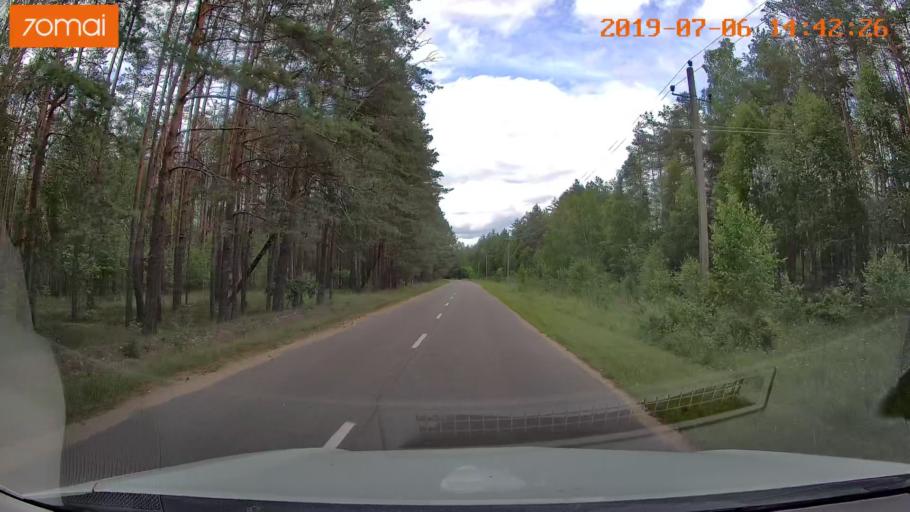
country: BY
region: Minsk
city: Ivyanyets
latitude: 53.9412
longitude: 26.6889
